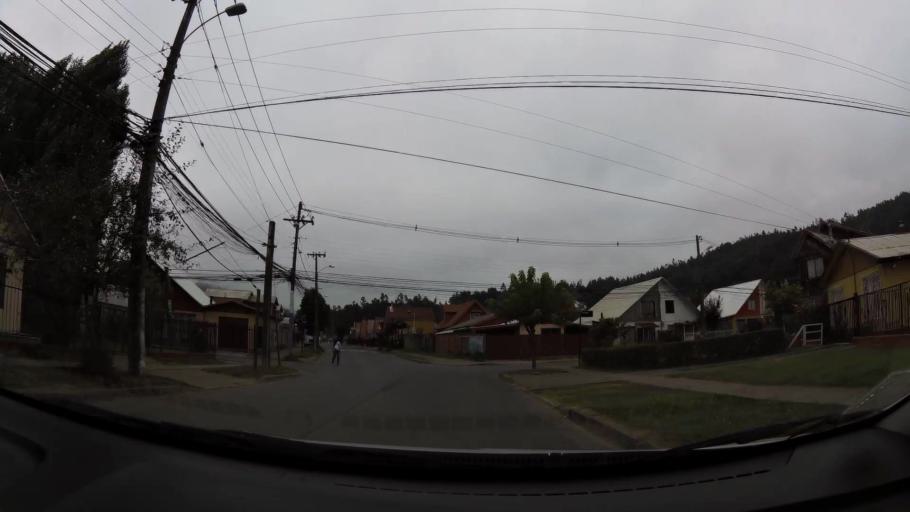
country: CL
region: Biobio
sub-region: Provincia de Concepcion
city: Concepcion
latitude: -36.8307
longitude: -73.0110
